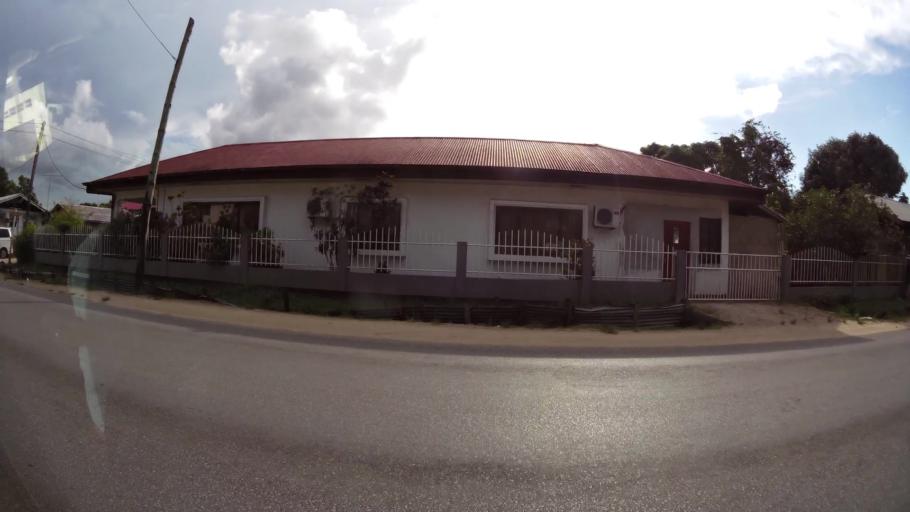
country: SR
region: Paramaribo
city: Paramaribo
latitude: 5.8455
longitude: -55.1811
